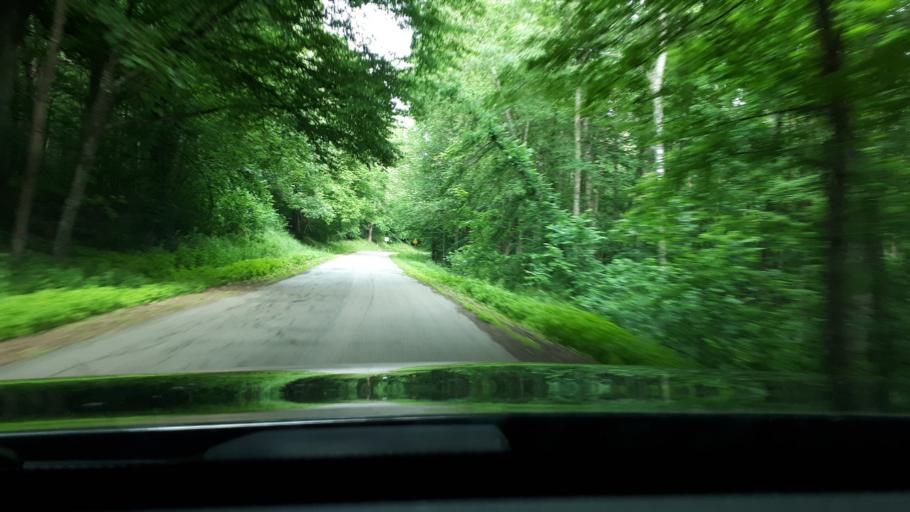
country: PL
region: Warmian-Masurian Voivodeship
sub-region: Powiat ostrodzki
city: Gierzwald
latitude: 53.6329
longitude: 20.1277
